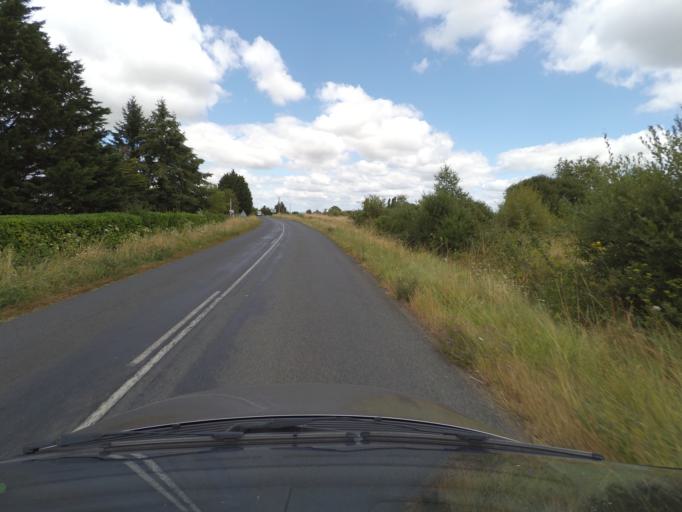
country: FR
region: Pays de la Loire
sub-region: Departement de Maine-et-Loire
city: Gennes
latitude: 47.3300
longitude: -0.2364
